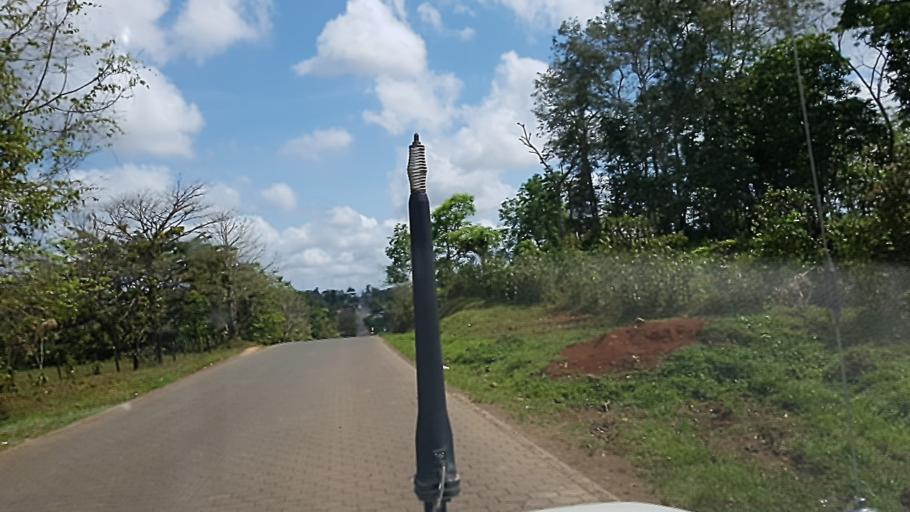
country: NI
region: Atlantico Sur
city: Nueva Guinea
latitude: 11.6805
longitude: -84.4499
